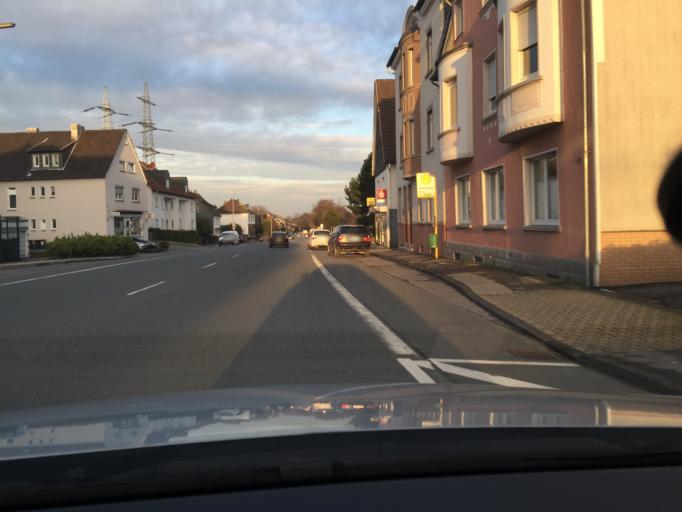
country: DE
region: North Rhine-Westphalia
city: Sprockhovel
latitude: 51.3160
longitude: 7.2511
